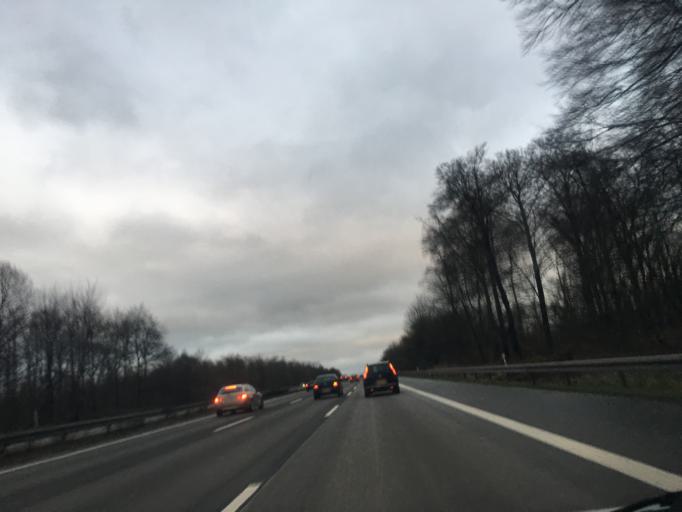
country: DE
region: North Rhine-Westphalia
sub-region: Regierungsbezirk Dusseldorf
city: Ratingen
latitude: 51.3360
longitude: 6.8771
